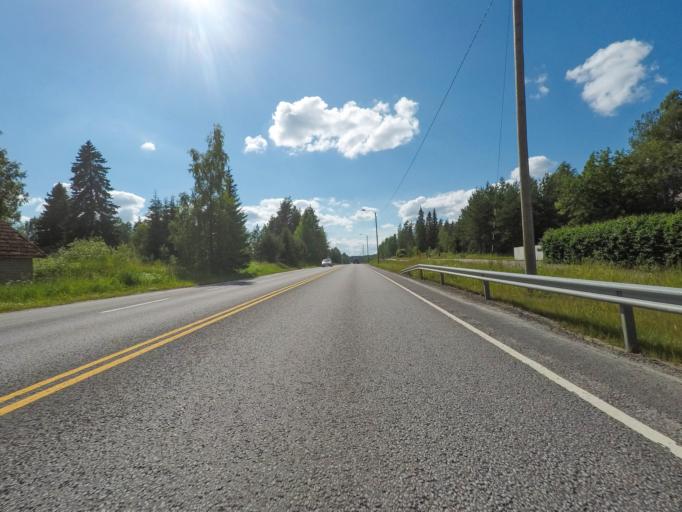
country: FI
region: Southern Savonia
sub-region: Savonlinna
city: Savonlinna
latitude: 61.8807
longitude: 29.0381
